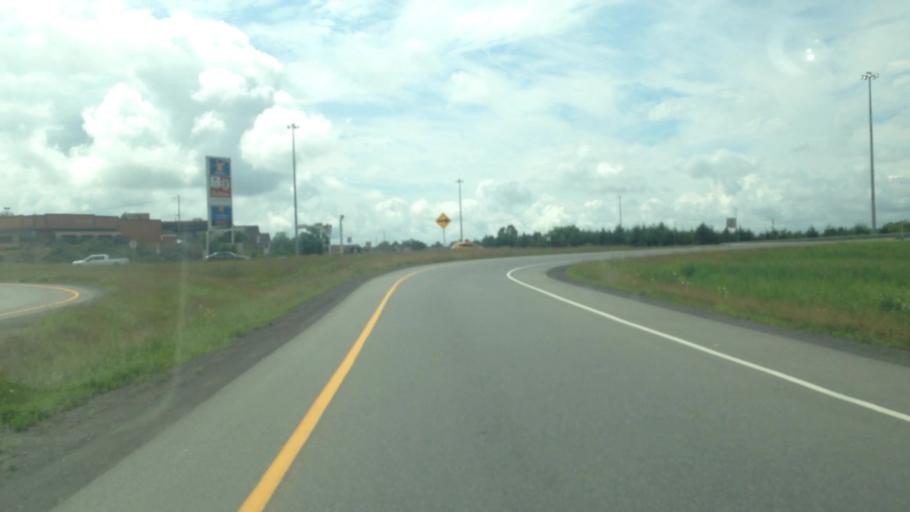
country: CA
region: Quebec
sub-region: Laurentides
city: Saint-Jerome
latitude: 45.7803
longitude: -74.0183
